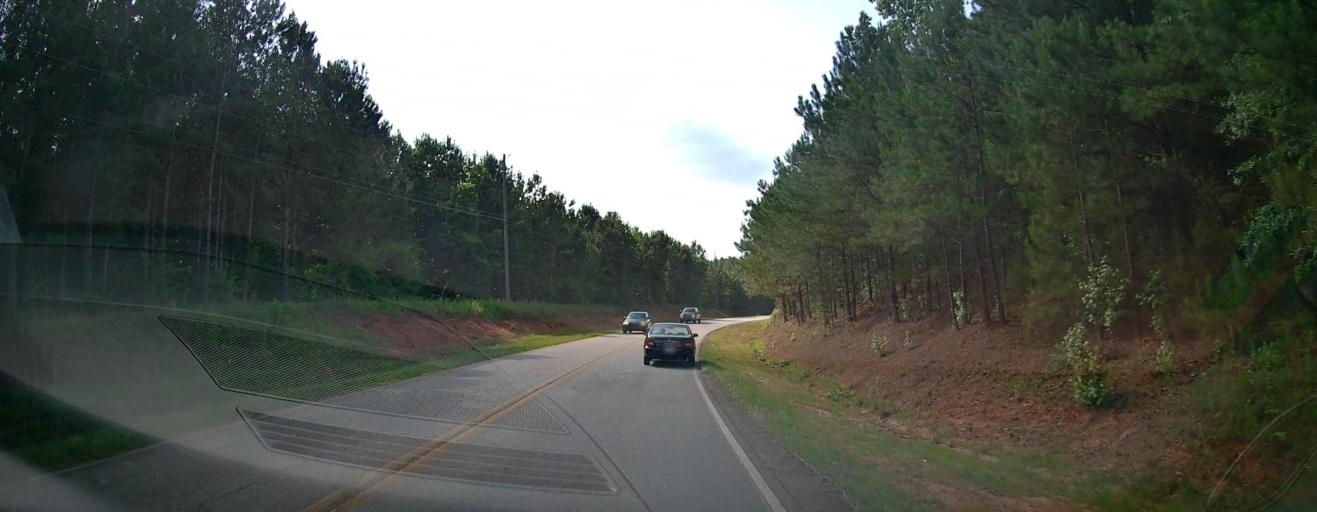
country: US
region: Georgia
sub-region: Henry County
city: McDonough
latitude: 33.4425
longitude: -84.2120
